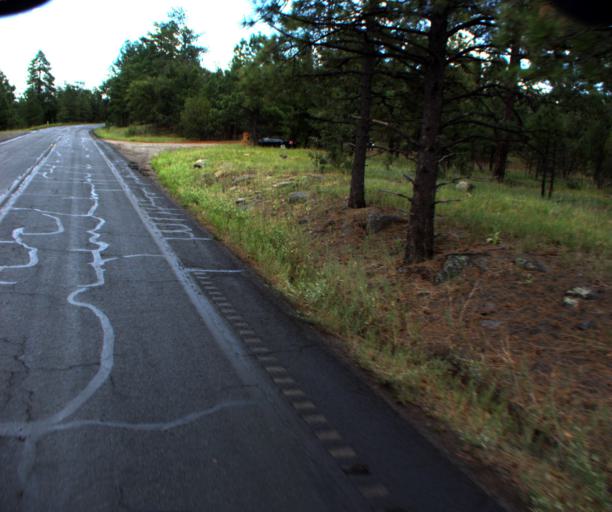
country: US
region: Arizona
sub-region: Gila County
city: Pine
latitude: 34.5134
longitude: -111.4861
